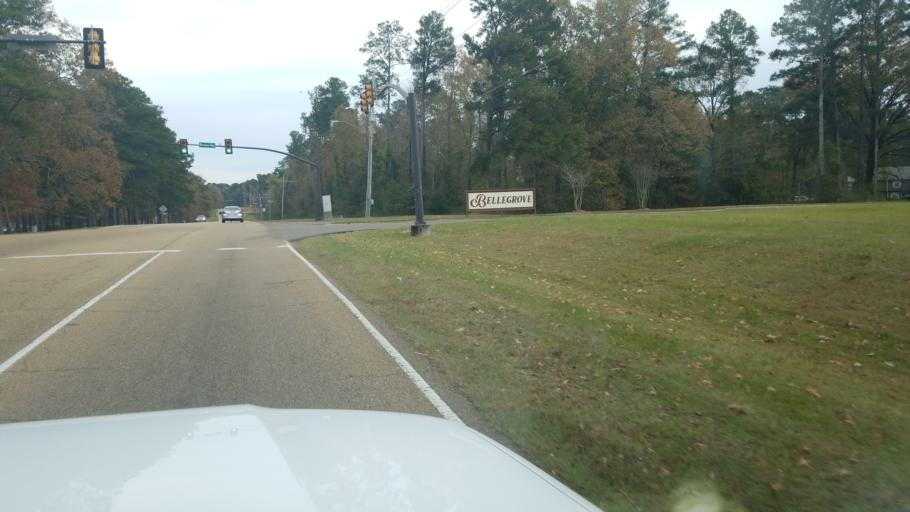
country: US
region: Mississippi
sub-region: Rankin County
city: Brandon
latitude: 32.3751
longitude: -90.0234
